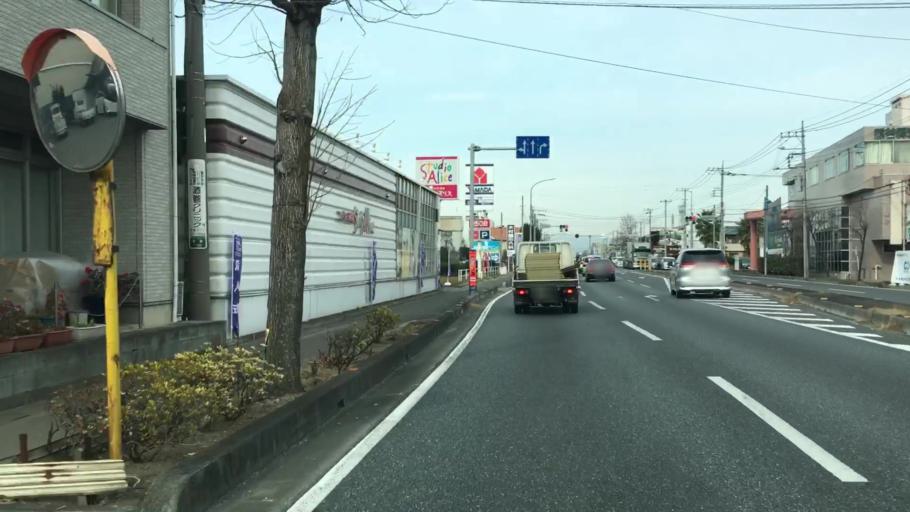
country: JP
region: Saitama
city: Kumagaya
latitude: 36.1612
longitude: 139.3708
